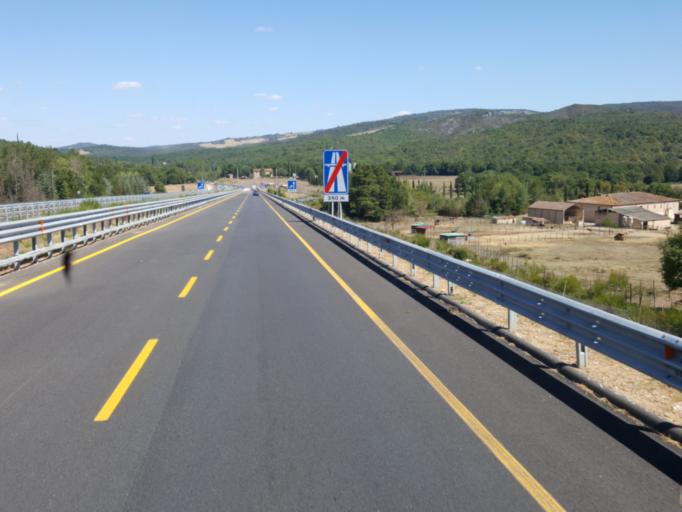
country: IT
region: Tuscany
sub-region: Provincia di Siena
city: Murlo
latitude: 43.1115
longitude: 11.2960
